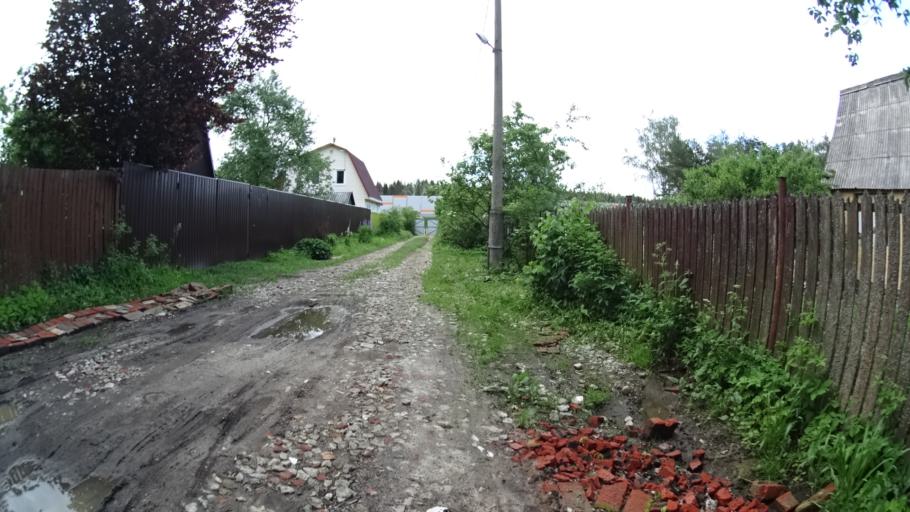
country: RU
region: Moskovskaya
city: Zelenogradskiy
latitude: 56.1242
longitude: 37.9070
